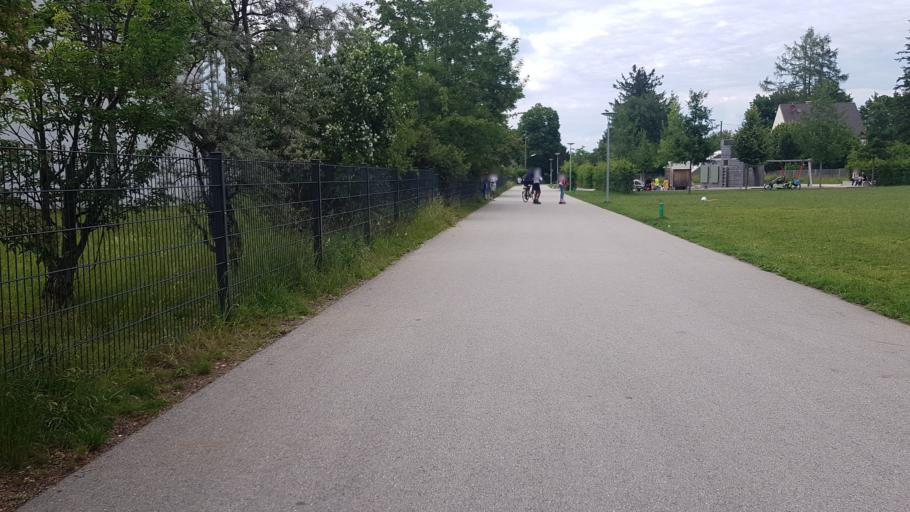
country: DE
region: Bavaria
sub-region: Upper Bavaria
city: Pasing
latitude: 48.1559
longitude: 11.4286
